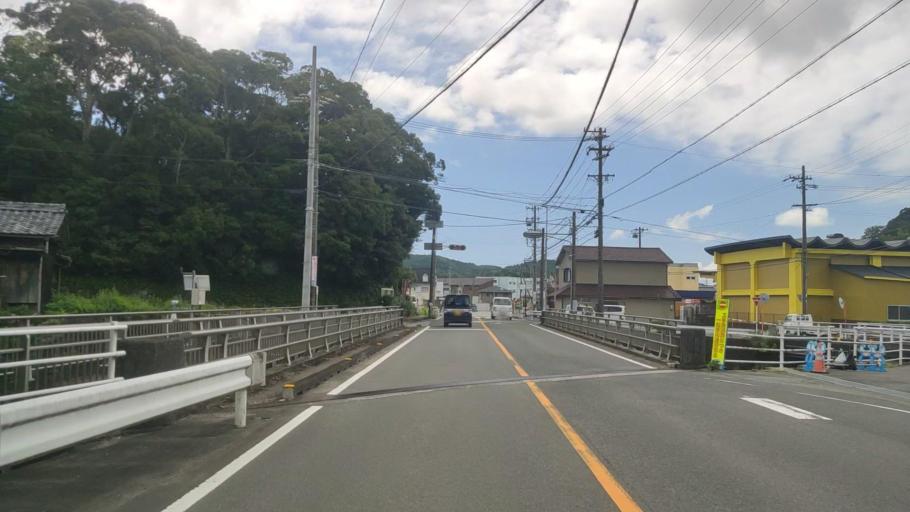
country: JP
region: Mie
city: Toba
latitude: 34.4472
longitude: 136.8437
